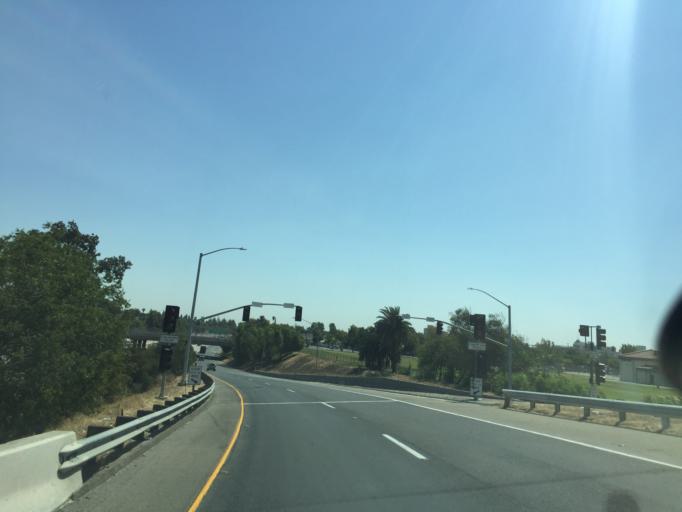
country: US
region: California
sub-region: Fresno County
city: Fresno
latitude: 36.7531
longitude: -119.7765
